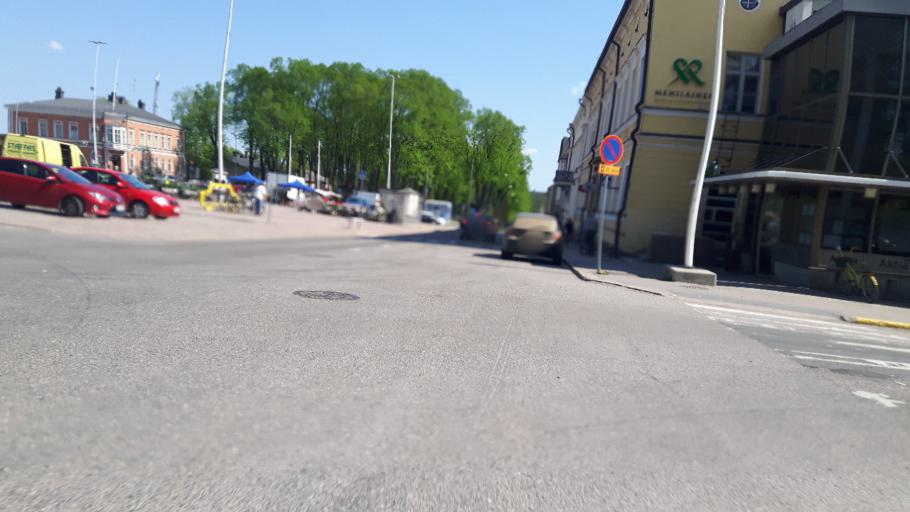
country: FI
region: Uusimaa
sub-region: Loviisa
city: Lovisa
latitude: 60.4565
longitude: 26.2249
